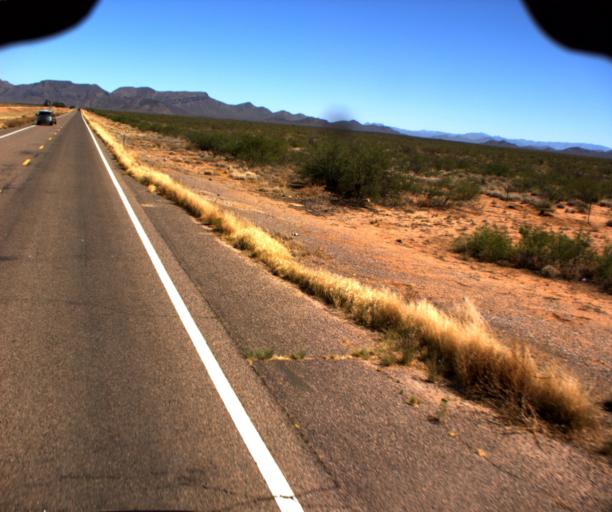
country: US
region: Arizona
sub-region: Yavapai County
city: Congress
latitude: 33.9538
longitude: -113.1416
